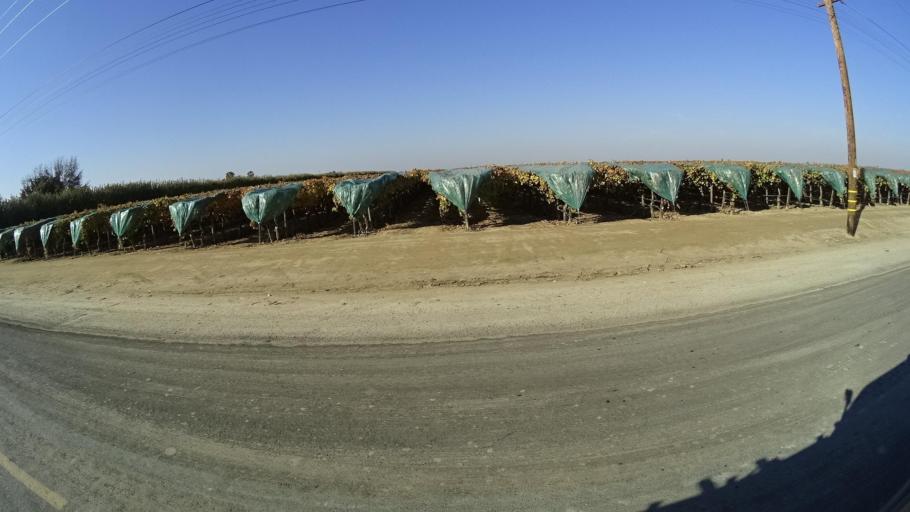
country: US
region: California
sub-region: Tulare County
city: Richgrove
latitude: 35.7510
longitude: -119.1342
